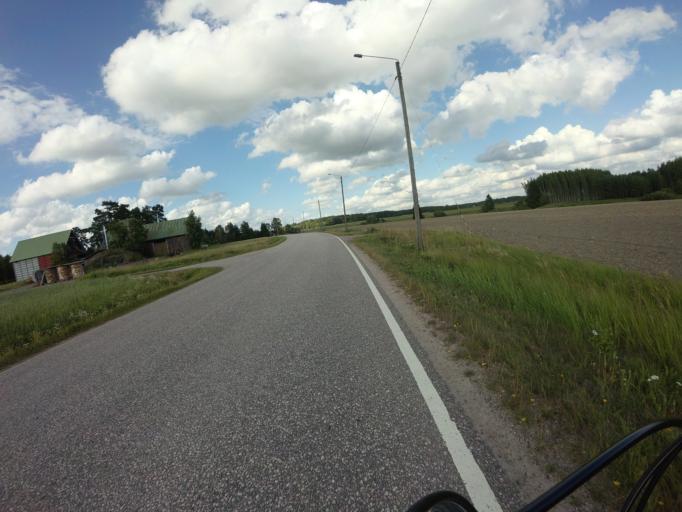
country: FI
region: Varsinais-Suomi
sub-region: Turku
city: Vahto
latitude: 60.5589
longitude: 22.3476
